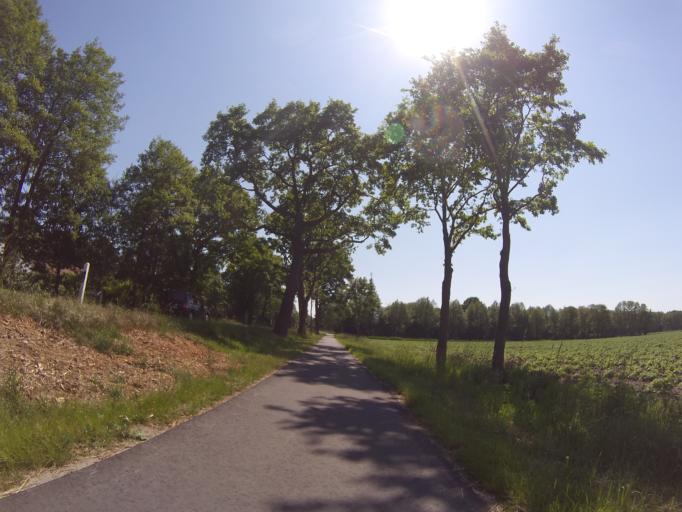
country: DE
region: Lower Saxony
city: Emlichheim
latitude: 52.6218
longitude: 6.8568
